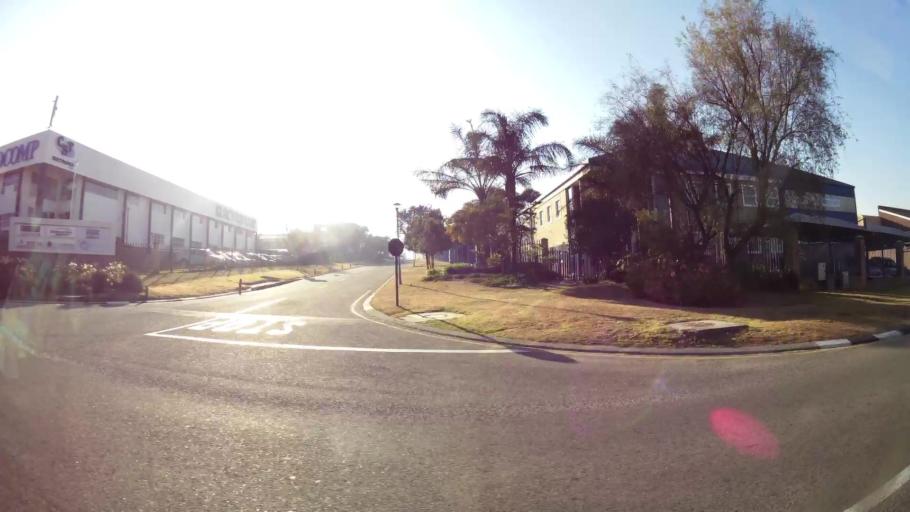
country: ZA
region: Gauteng
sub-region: City of Johannesburg Metropolitan Municipality
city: Modderfontein
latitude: -26.0728
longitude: 28.1140
